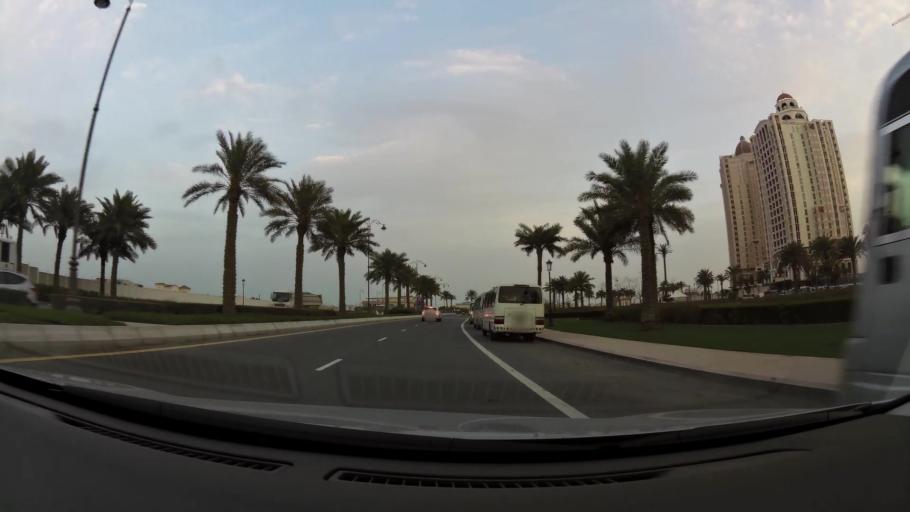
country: QA
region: Baladiyat ad Dawhah
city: Doha
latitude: 25.3707
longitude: 51.5604
